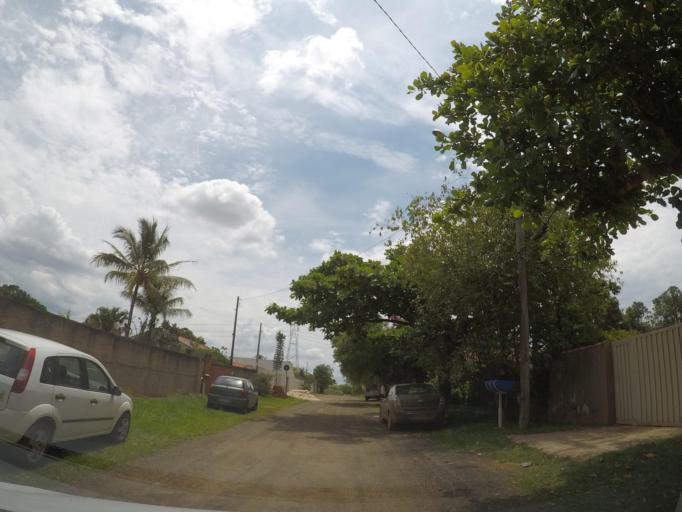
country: BR
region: Sao Paulo
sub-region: Sumare
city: Sumare
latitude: -22.8478
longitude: -47.2948
